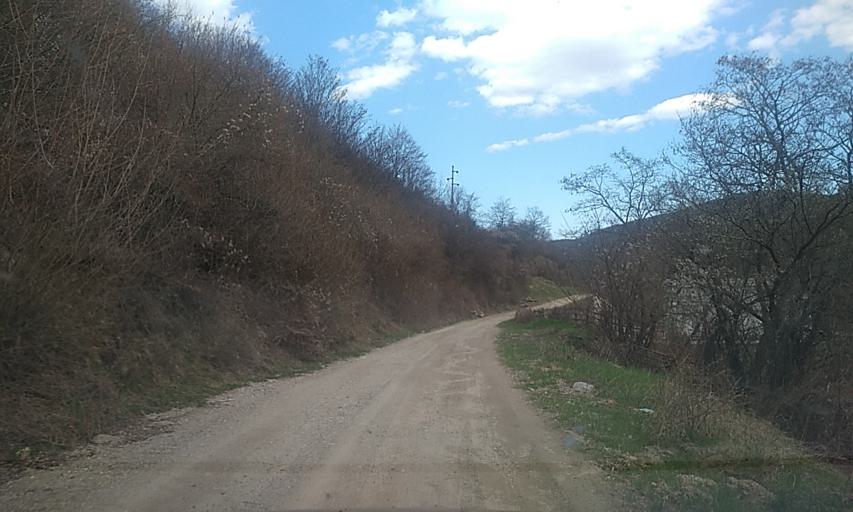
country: MK
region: Kriva Palanka
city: Kriva Palanka
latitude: 42.3410
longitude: 22.3716
